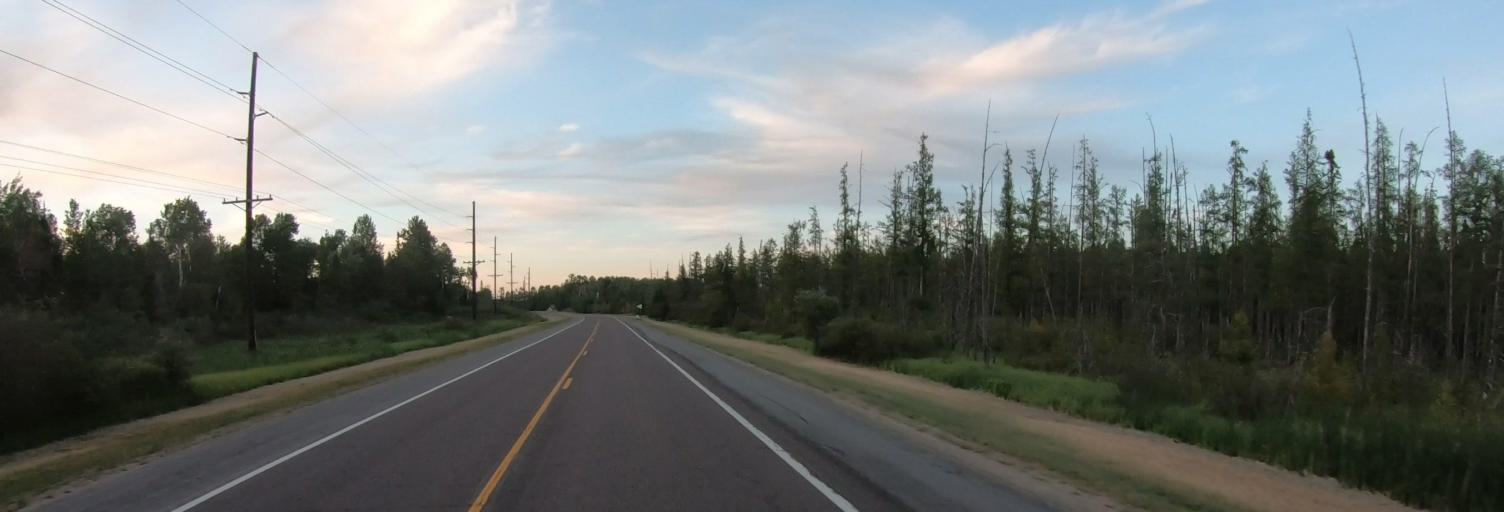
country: US
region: Minnesota
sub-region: Saint Louis County
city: Aurora
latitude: 47.8108
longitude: -92.3718
